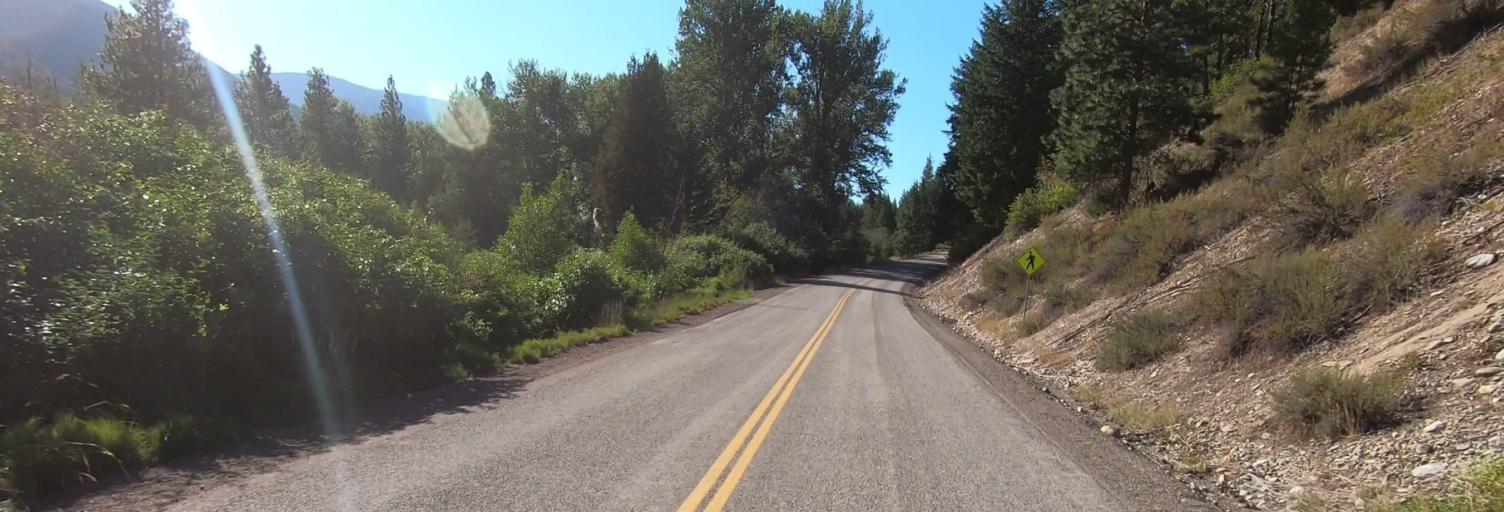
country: US
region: Washington
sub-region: Chelan County
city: Granite Falls
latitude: 48.5585
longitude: -120.3425
